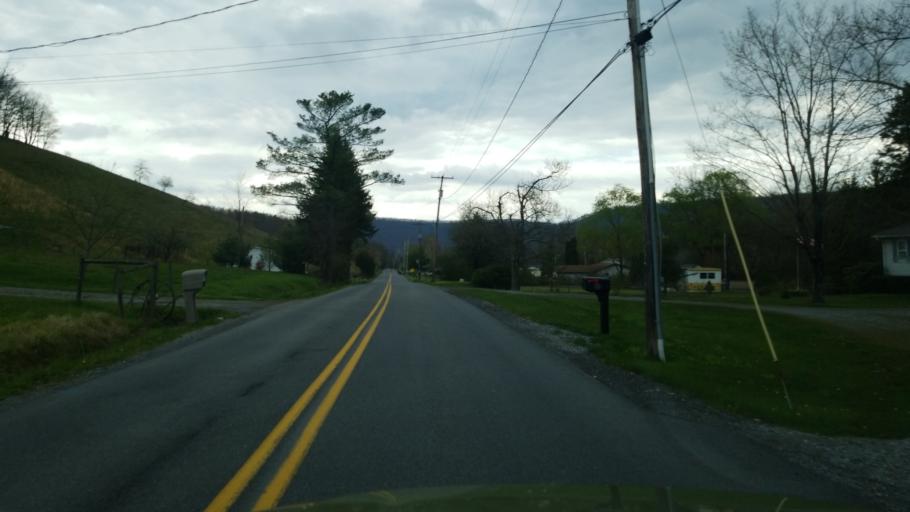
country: US
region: Pennsylvania
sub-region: Blair County
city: Tipton
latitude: 40.6460
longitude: -78.3156
